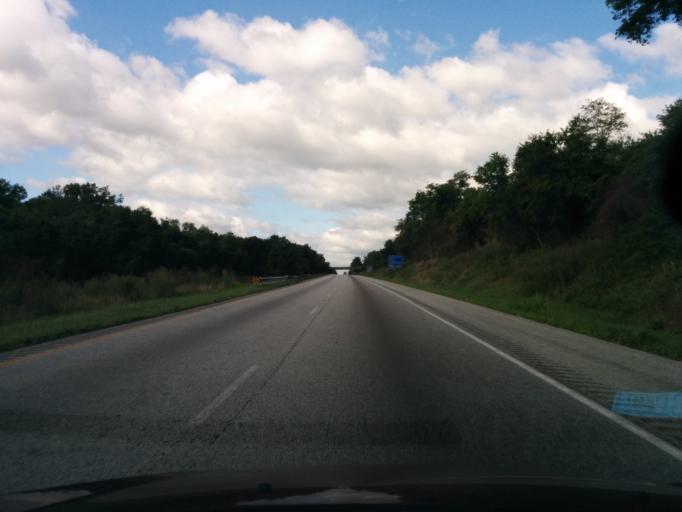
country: US
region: Virginia
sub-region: Rockbridge County
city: Glasgow
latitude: 37.6905
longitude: -79.4833
